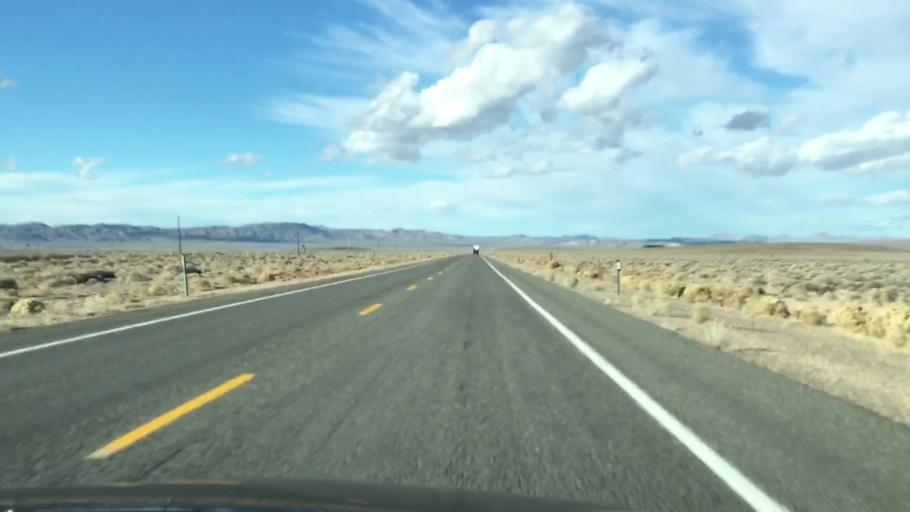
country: US
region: Nevada
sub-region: Esmeralda County
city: Goldfield
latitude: 37.4082
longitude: -117.1517
